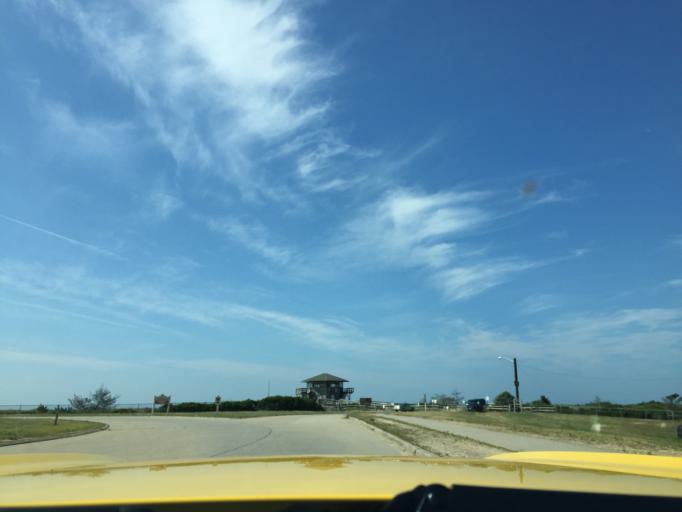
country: US
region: New York
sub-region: Suffolk County
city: Mastic Beach
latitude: 40.7337
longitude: -72.8661
